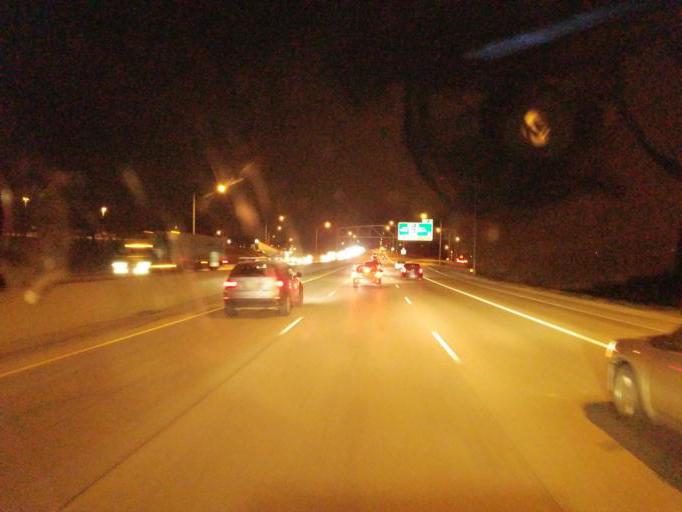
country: US
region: Iowa
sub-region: Polk County
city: Clive
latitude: 41.5923
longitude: -93.7420
